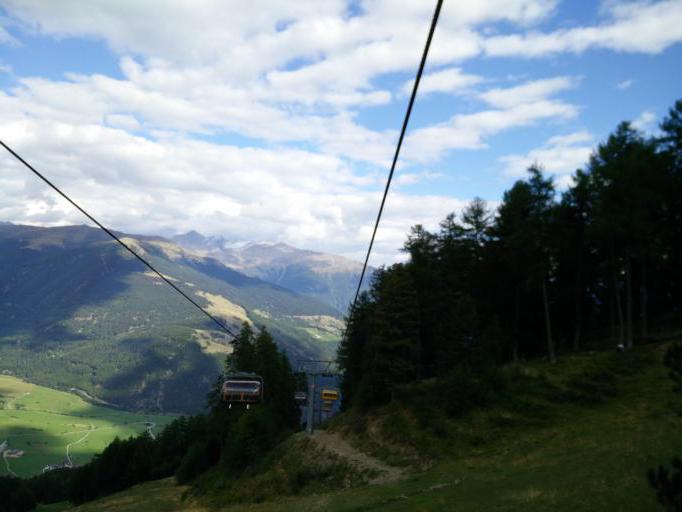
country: IT
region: Trentino-Alto Adige
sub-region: Bolzano
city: Malles Venosta
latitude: 46.7055
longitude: 10.5020
